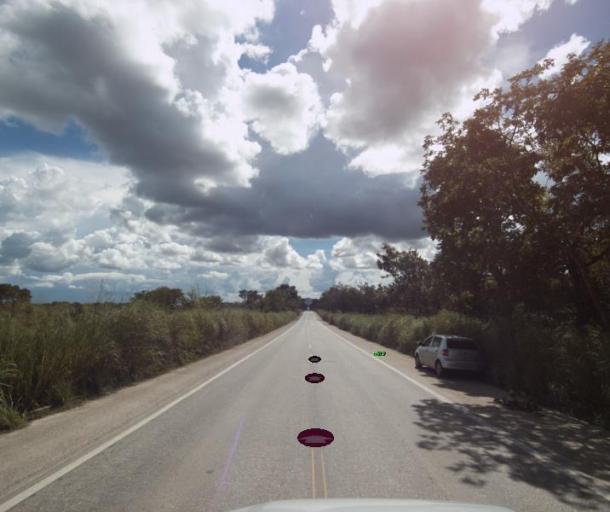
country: BR
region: Goias
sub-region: Porangatu
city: Porangatu
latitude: -13.5558
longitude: -49.0690
